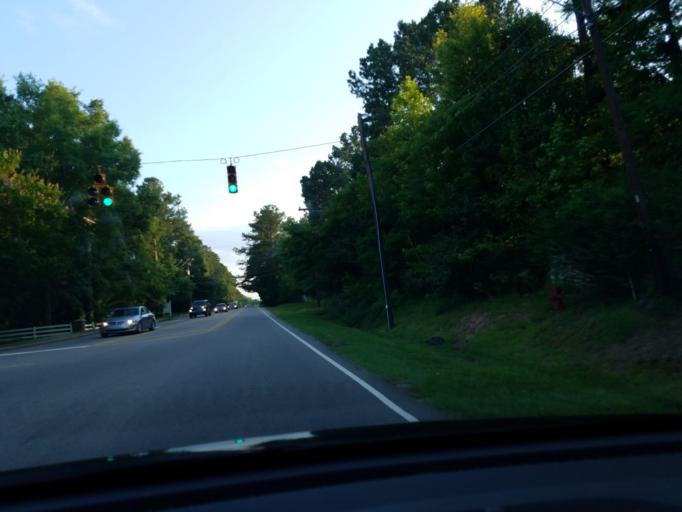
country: US
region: North Carolina
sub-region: Durham County
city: Durham
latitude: 35.9270
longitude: -78.9538
